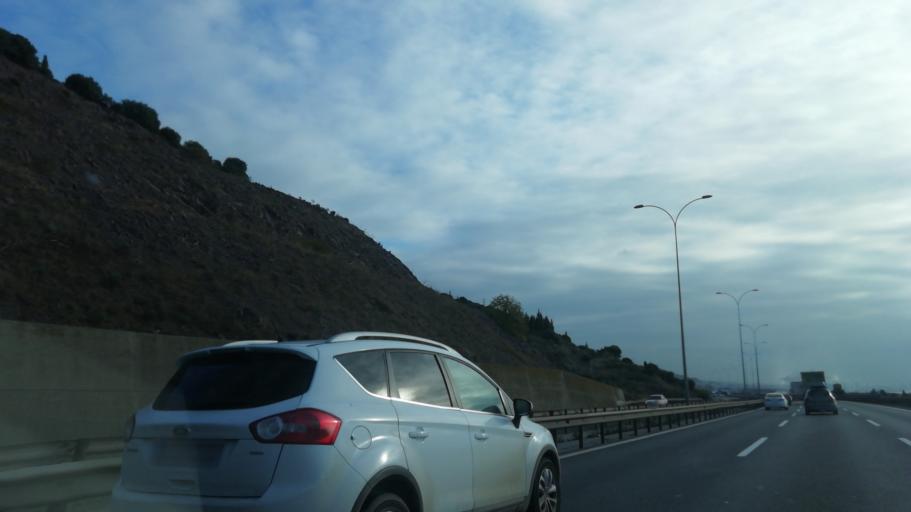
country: TR
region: Kocaeli
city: Hereke
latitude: 40.7791
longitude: 29.6737
